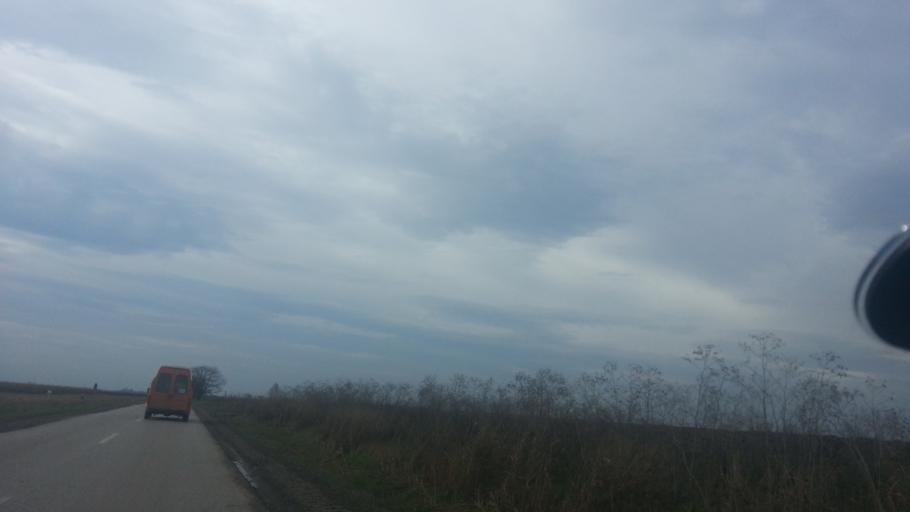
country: RS
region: Autonomna Pokrajina Vojvodina
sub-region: Sremski Okrug
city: Stara Pazova
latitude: 44.9822
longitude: 20.1122
